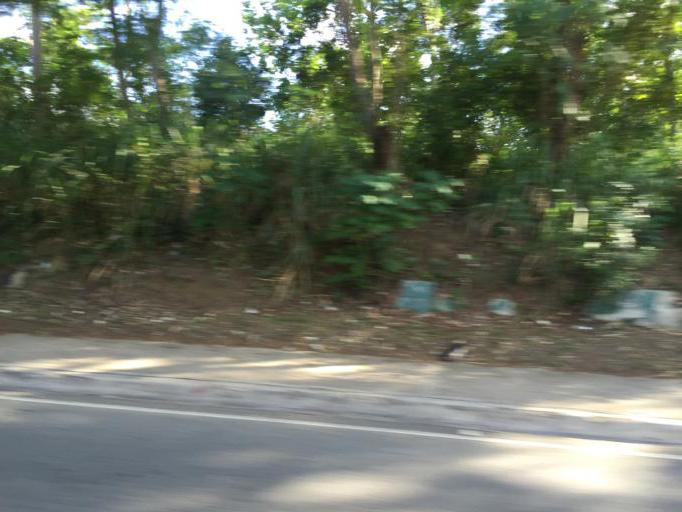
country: DO
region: Nacional
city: La Agustina
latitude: 18.4889
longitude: -69.9535
